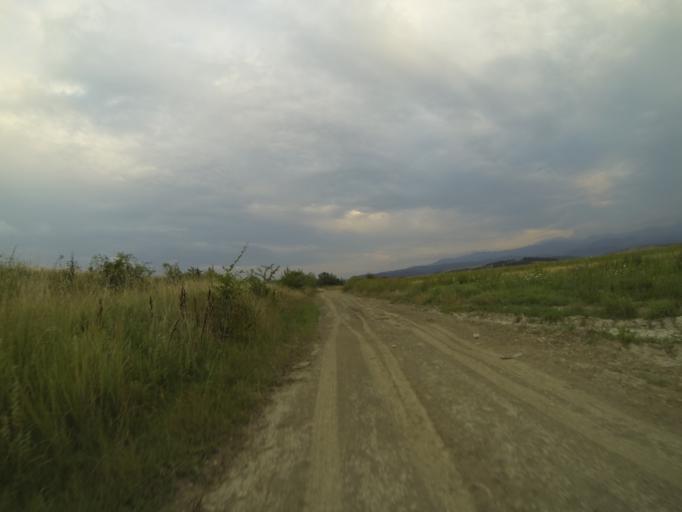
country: RO
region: Brasov
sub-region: Comuna Sinca Veche
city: Sinca Veche
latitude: 45.7742
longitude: 25.1677
